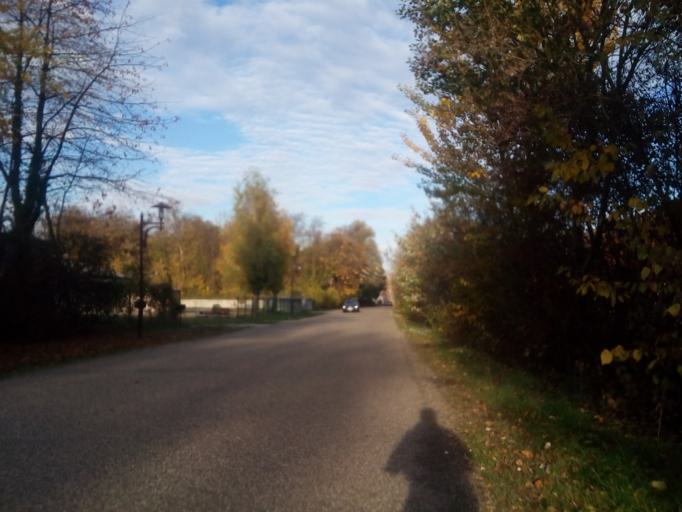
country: FR
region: Alsace
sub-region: Departement du Bas-Rhin
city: Herrlisheim
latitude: 48.7061
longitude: 7.9163
